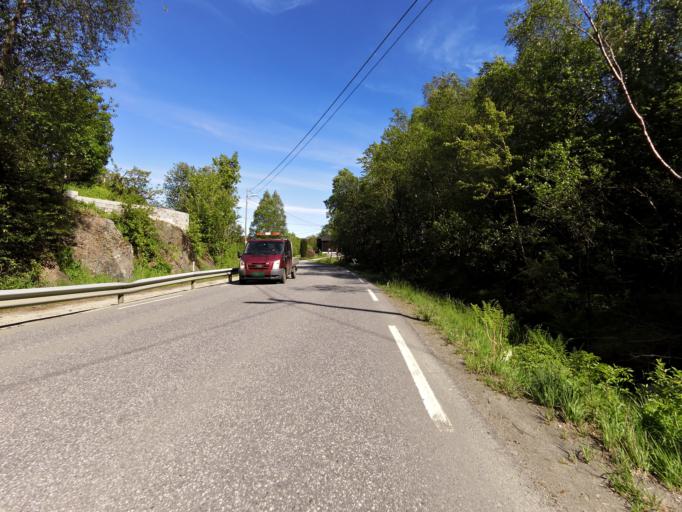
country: NO
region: Hordaland
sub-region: Stord
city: Sagvag
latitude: 59.7821
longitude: 5.4033
